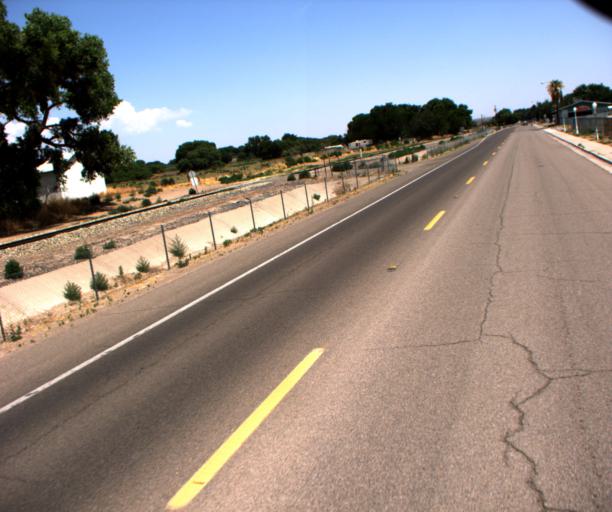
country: US
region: Arizona
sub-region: Greenlee County
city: Clifton
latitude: 32.7261
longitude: -109.1085
